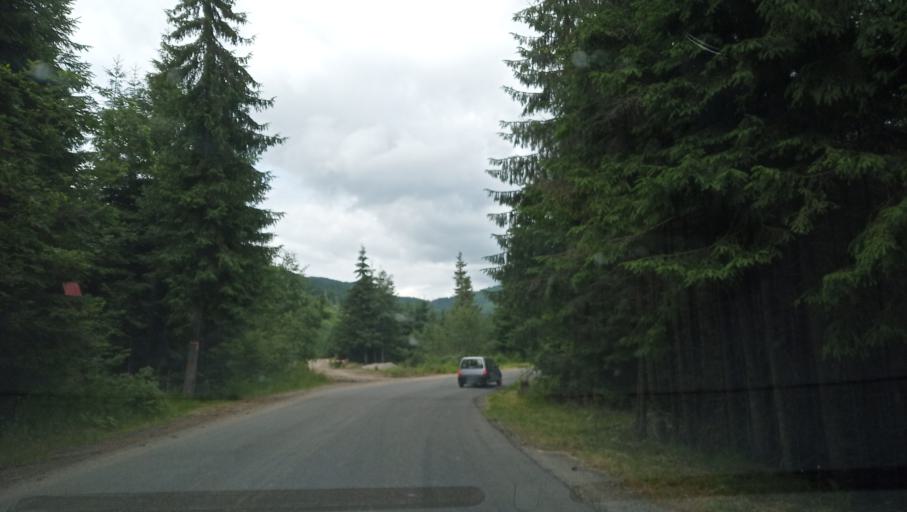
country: RO
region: Gorj
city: Novaci-Straini
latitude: 45.4310
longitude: 23.6690
